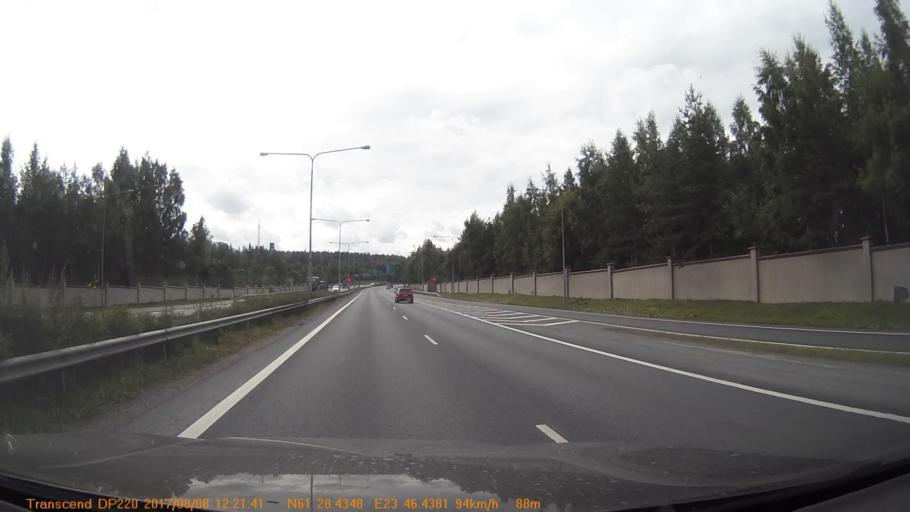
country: FI
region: Pirkanmaa
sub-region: Tampere
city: Tampere
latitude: 61.4736
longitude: 23.7739
